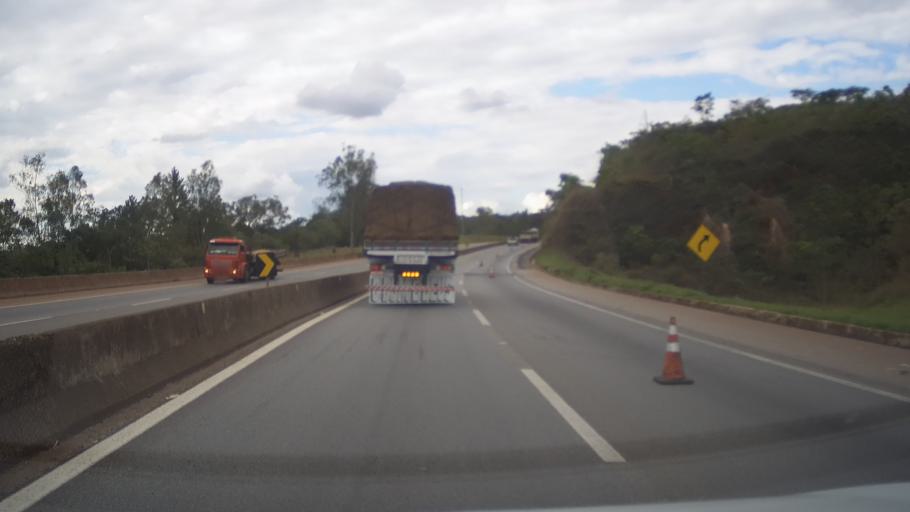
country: BR
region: Minas Gerais
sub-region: Itauna
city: Itauna
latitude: -20.3238
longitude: -44.4567
